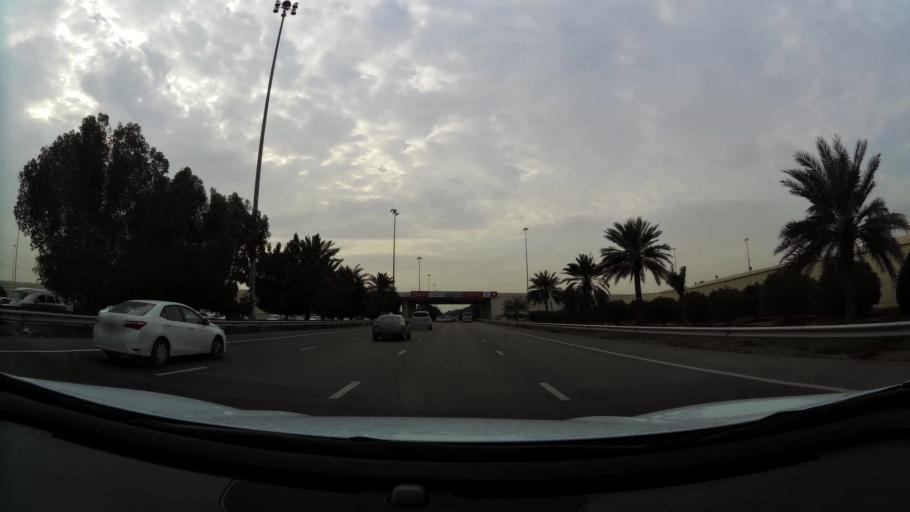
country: AE
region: Abu Dhabi
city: Abu Dhabi
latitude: 24.3532
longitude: 54.5685
